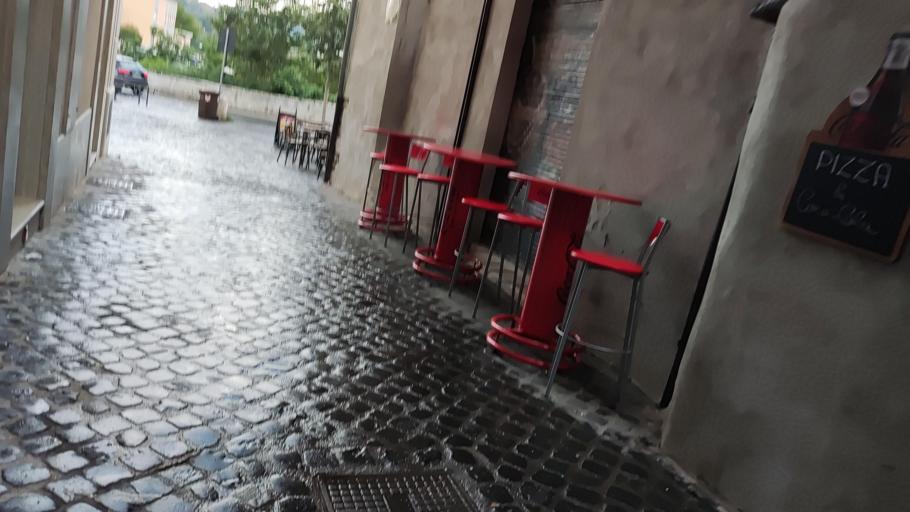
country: IT
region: Latium
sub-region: Citta metropolitana di Roma Capitale
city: Tivoli
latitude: 41.9658
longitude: 12.7996
